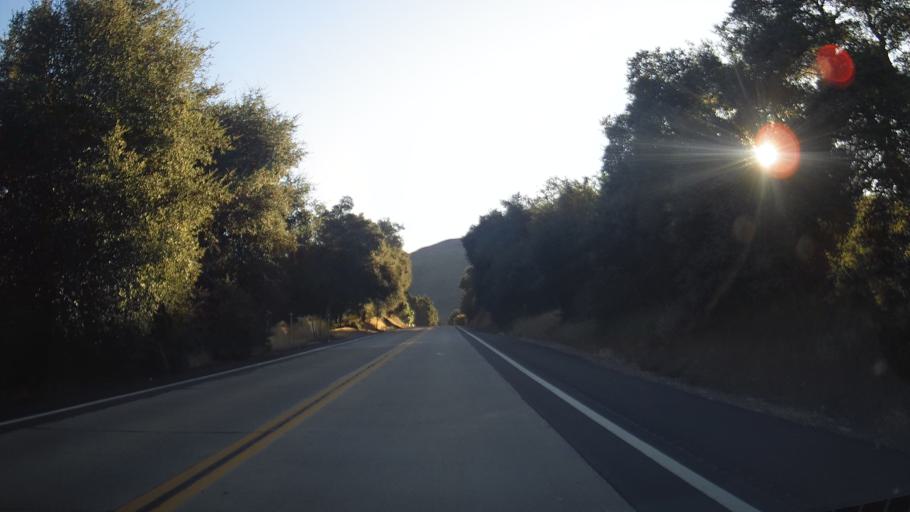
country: US
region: California
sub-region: San Diego County
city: Descanso
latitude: 32.8419
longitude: -116.6081
